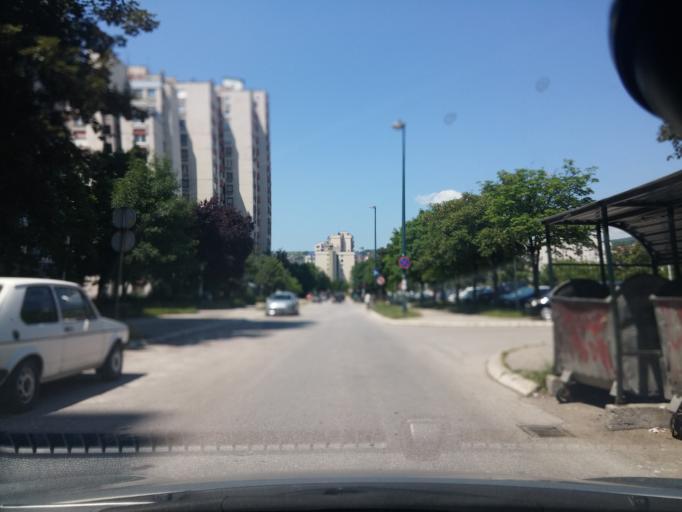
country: BA
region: Federation of Bosnia and Herzegovina
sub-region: Kanton Sarajevo
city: Sarajevo
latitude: 43.8415
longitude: 18.3479
